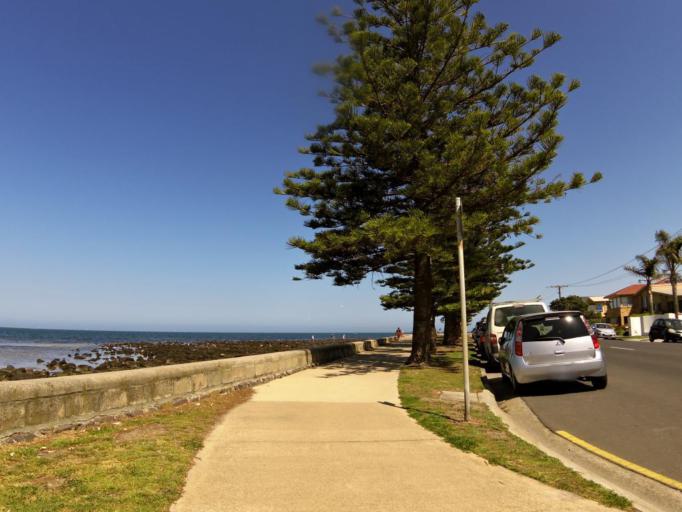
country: AU
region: Victoria
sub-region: Hobsons Bay
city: Seaholme
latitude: -37.8704
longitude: 144.8412
